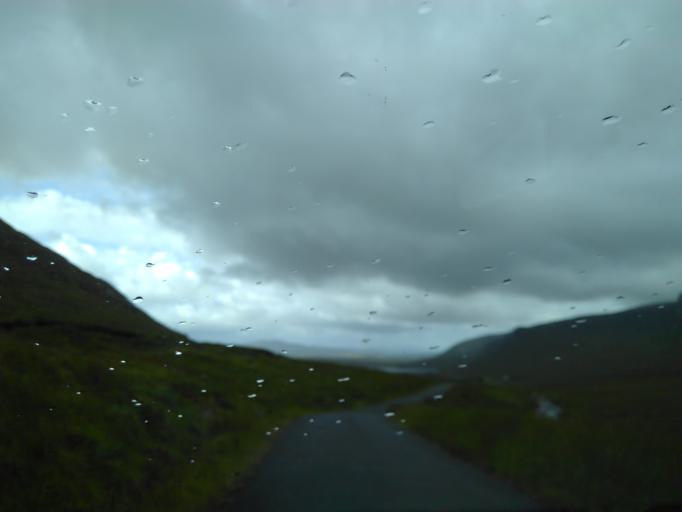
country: IE
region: Ulster
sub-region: County Donegal
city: Dunlewy
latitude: 54.9744
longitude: -8.0779
